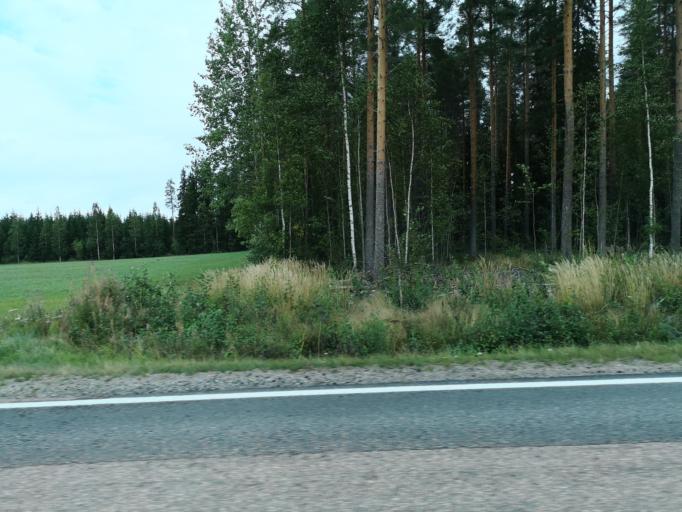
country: FI
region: Central Finland
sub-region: Jyvaeskylae
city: Hankasalmi
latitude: 62.3611
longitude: 26.5443
